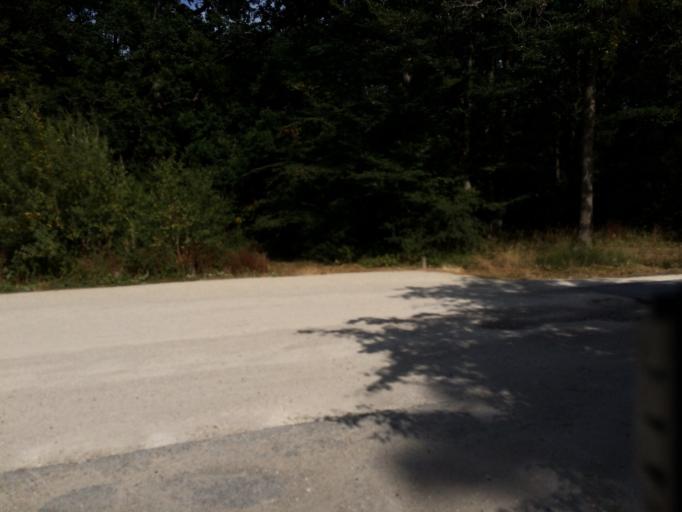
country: FR
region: Ile-de-France
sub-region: Departement de l'Essonne
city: Tigery
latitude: 48.6546
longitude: 2.4931
